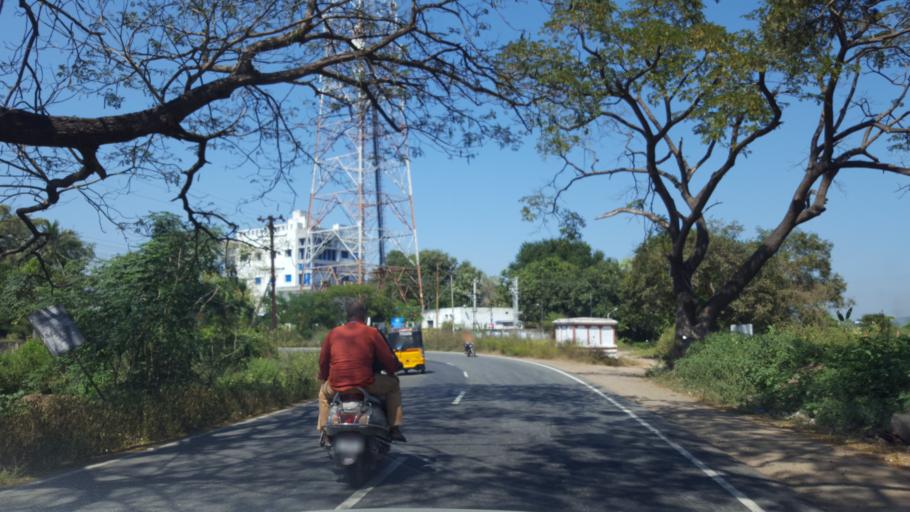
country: IN
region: Tamil Nadu
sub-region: Kancheepuram
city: Chengalpattu
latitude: 12.7349
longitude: 79.9441
